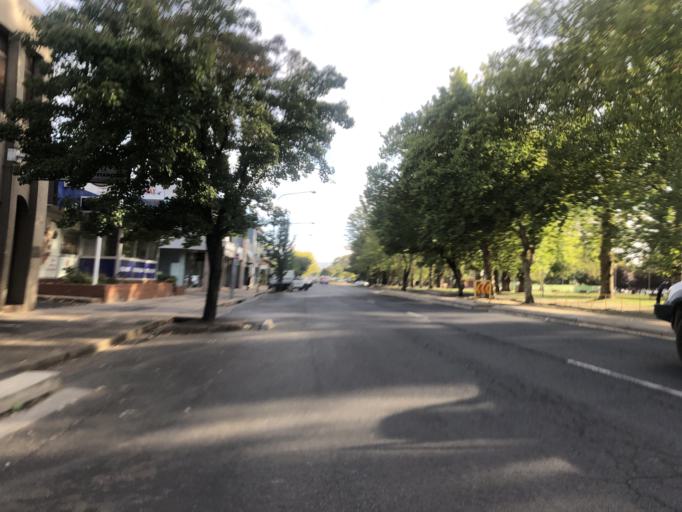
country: AU
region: New South Wales
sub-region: Orange Municipality
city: Orange
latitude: -33.2834
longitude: 149.1012
